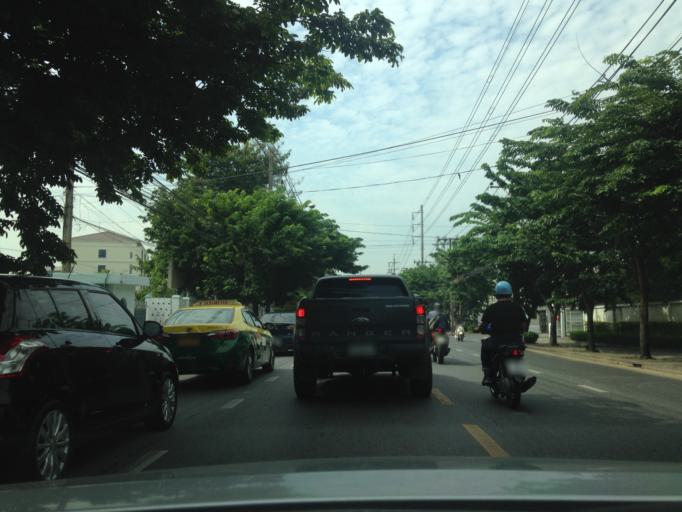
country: TH
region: Bangkok
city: Bang Phlat
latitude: 13.7933
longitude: 100.5178
